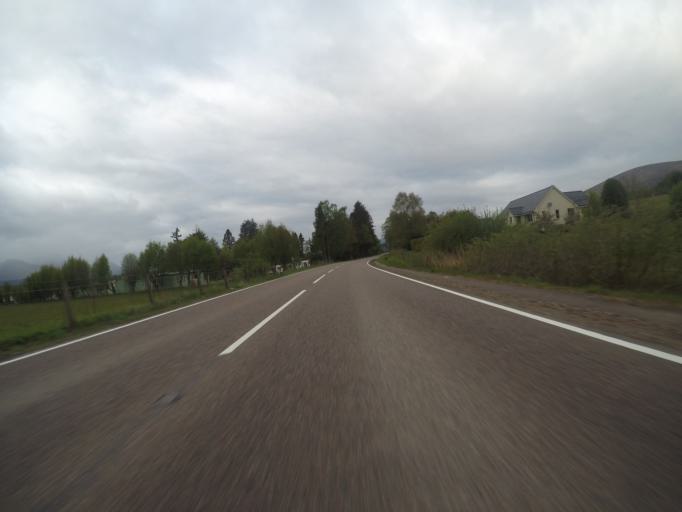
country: GB
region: Scotland
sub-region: Highland
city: Spean Bridge
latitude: 56.8895
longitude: -4.8600
